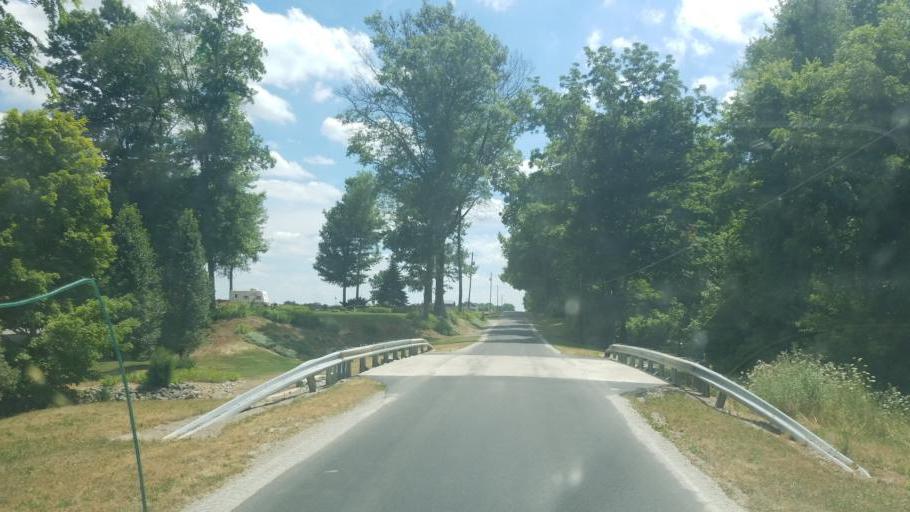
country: US
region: Ohio
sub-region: Defiance County
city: Hicksville
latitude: 41.3623
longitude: -84.6902
